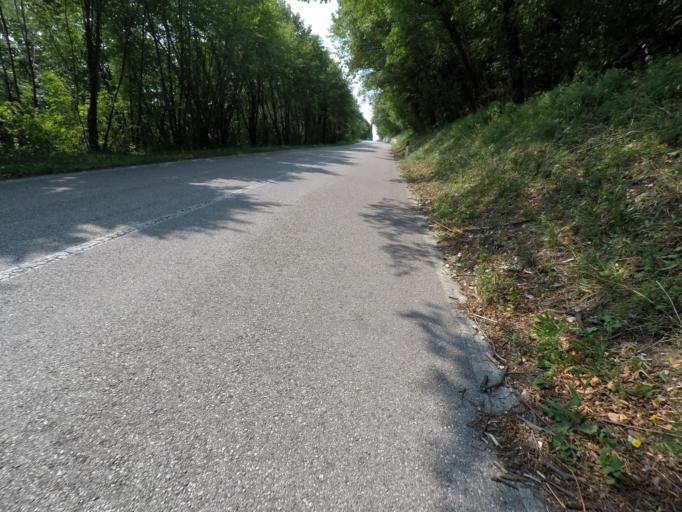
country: IT
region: Friuli Venezia Giulia
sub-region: Provincia di Pordenone
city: Montereale Valcellina
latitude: 46.1696
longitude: 12.6615
